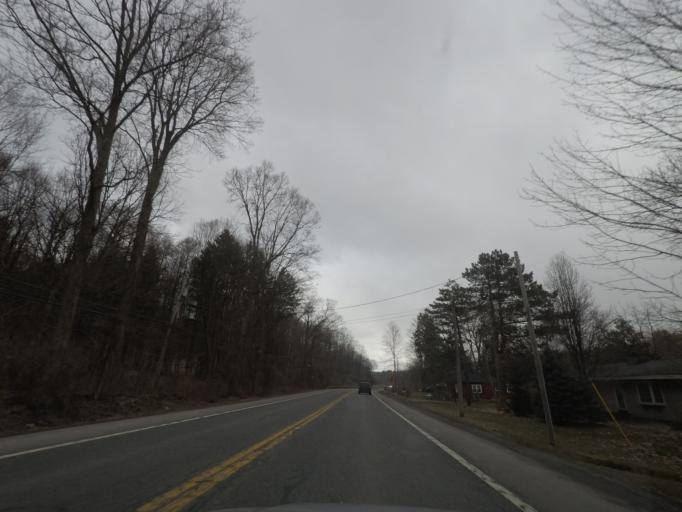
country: US
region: New York
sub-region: Onondaga County
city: Fayetteville
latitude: 43.0379
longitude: -75.9692
